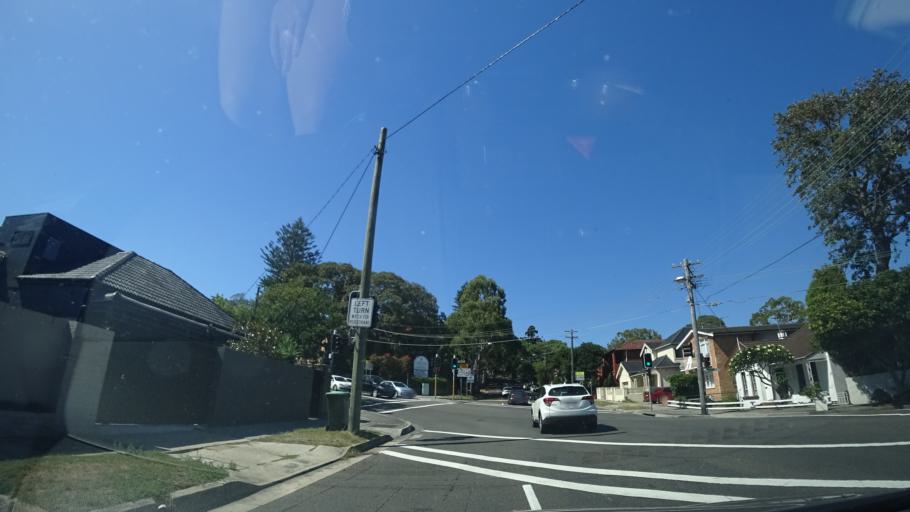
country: AU
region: New South Wales
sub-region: Randwick
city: Randwick
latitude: -33.9045
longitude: 151.2445
